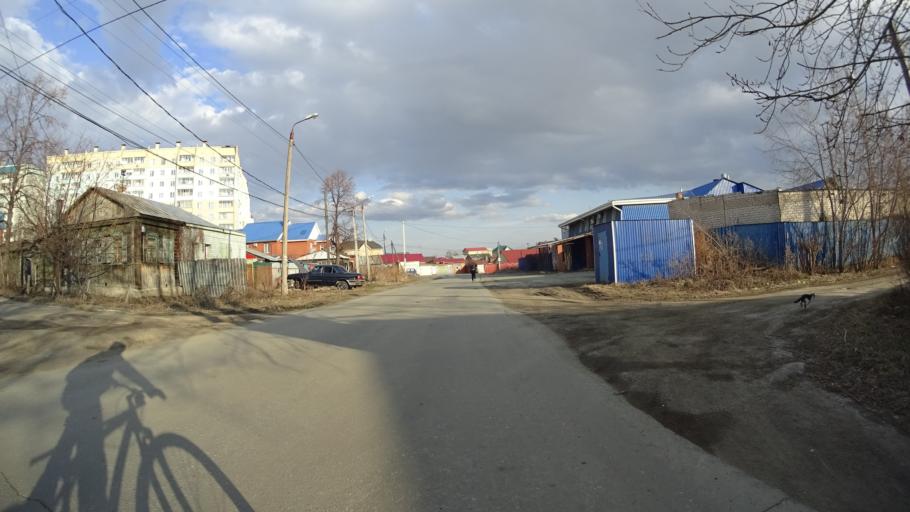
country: RU
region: Chelyabinsk
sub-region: Gorod Chelyabinsk
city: Chelyabinsk
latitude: 55.1369
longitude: 61.3959
